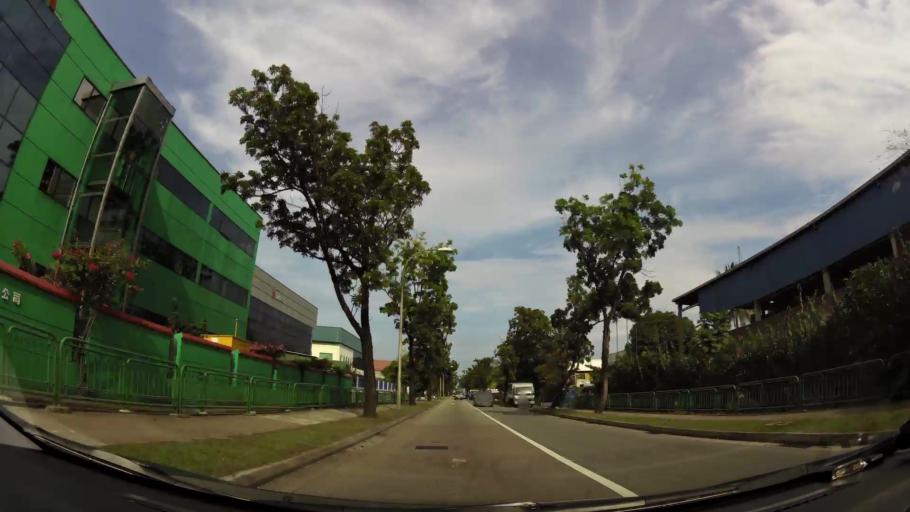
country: MY
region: Johor
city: Johor Bahru
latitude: 1.3152
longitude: 103.6536
